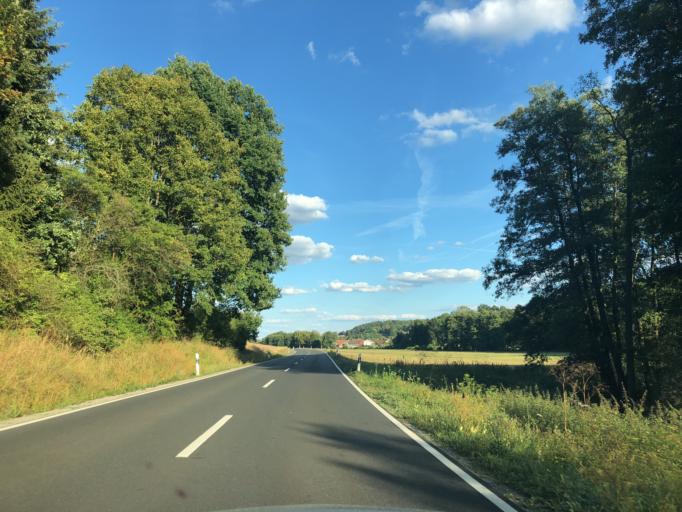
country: DE
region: Bavaria
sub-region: Upper Franconia
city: Burgwindheim
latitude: 49.8331
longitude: 10.5550
